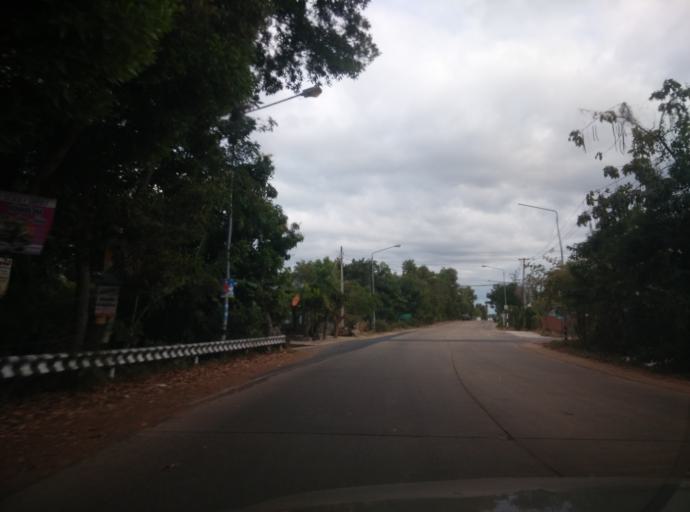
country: TH
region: Sisaket
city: Si Sa Ket
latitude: 15.1232
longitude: 104.3454
